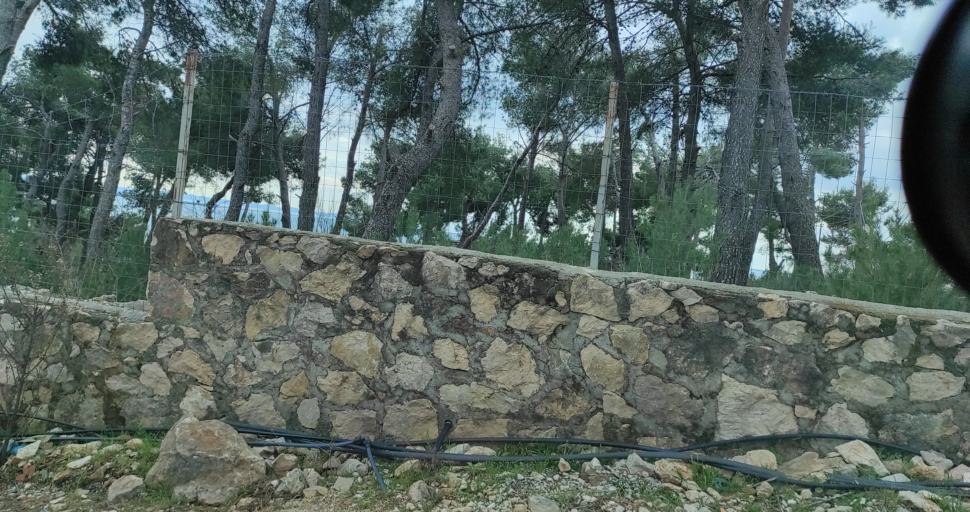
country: AL
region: Lezhe
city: Shengjin
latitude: 41.8124
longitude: 19.5829
